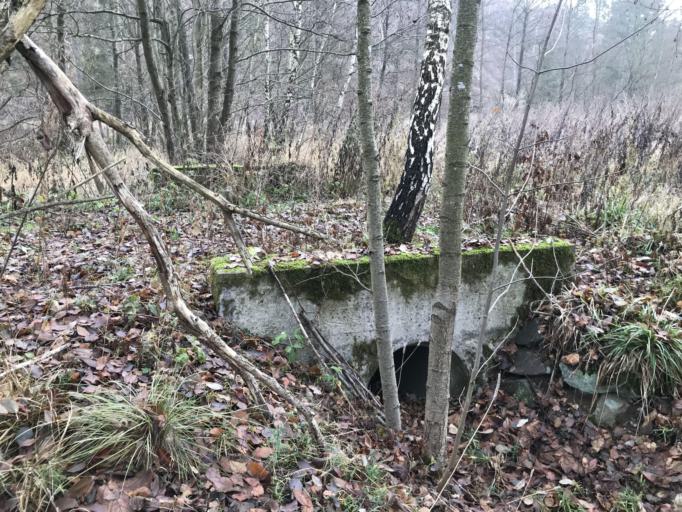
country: DE
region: Saxony-Anhalt
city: Friedrichsbrunn
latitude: 51.6654
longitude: 11.0515
